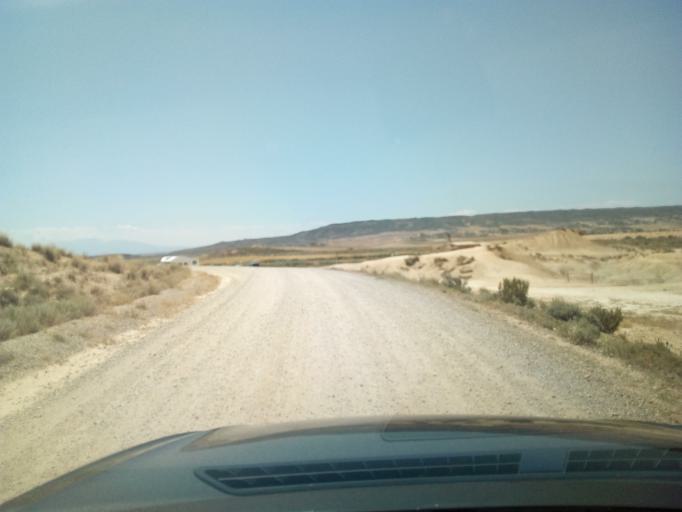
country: ES
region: Navarre
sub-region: Provincia de Navarra
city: Arguedas
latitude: 42.2101
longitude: -1.5146
